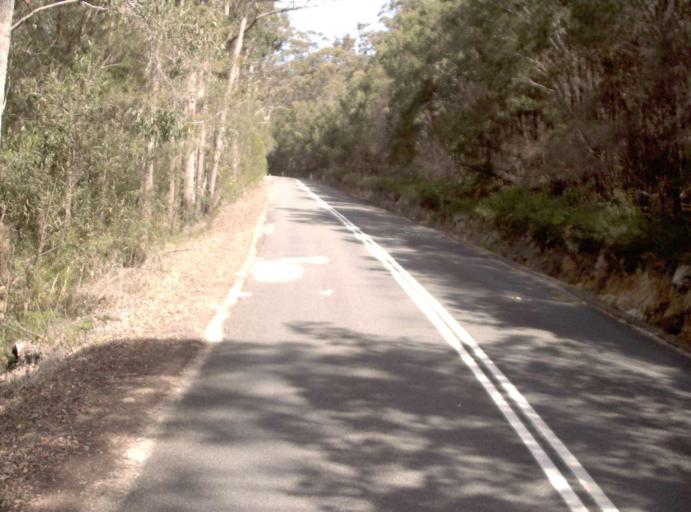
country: AU
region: New South Wales
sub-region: Bega Valley
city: Eden
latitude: -37.4980
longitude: 149.6744
